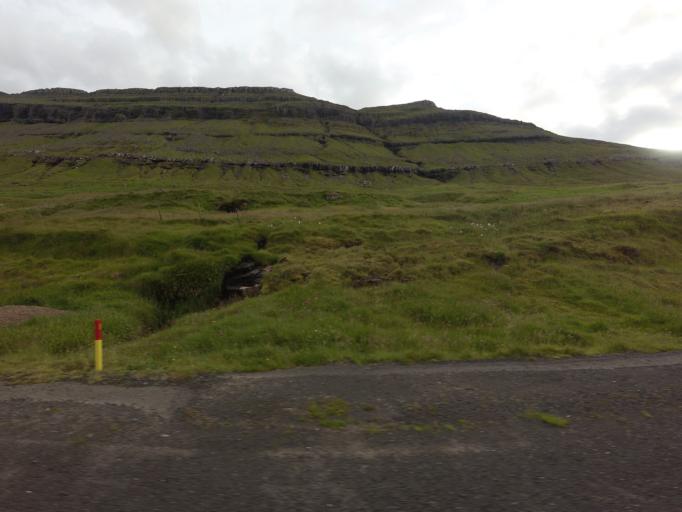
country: FO
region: Streymoy
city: Kollafjordhur
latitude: 62.1438
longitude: -6.9039
